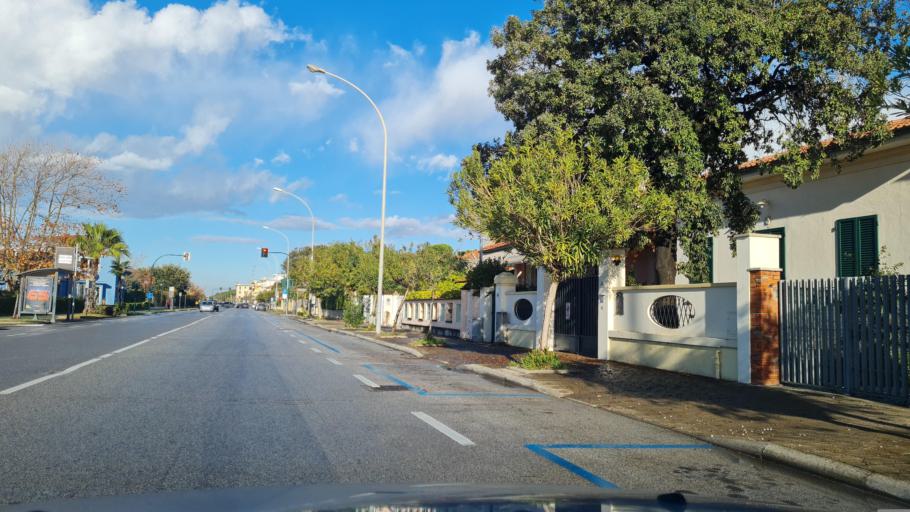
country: IT
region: Tuscany
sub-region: Provincia di Lucca
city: Pietrasanta
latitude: 43.9350
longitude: 10.1919
